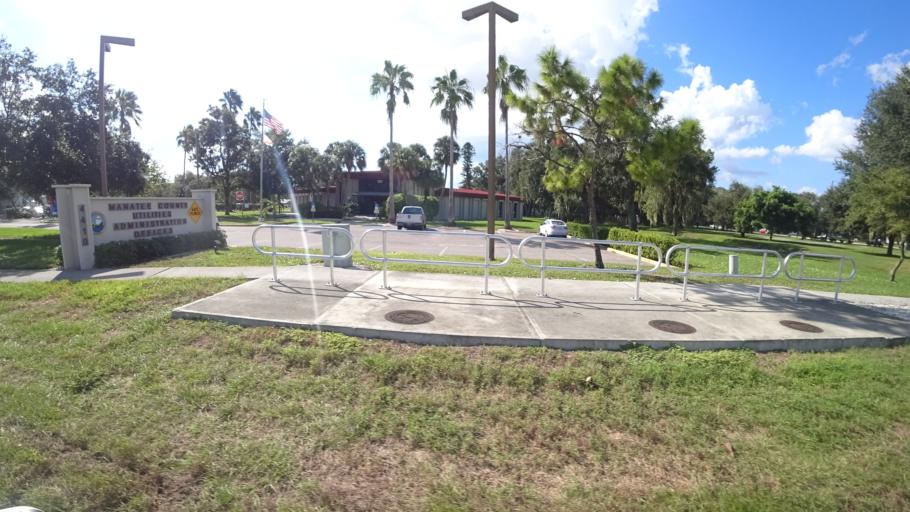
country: US
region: Florida
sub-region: Manatee County
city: West Bradenton
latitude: 27.4615
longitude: -82.6268
